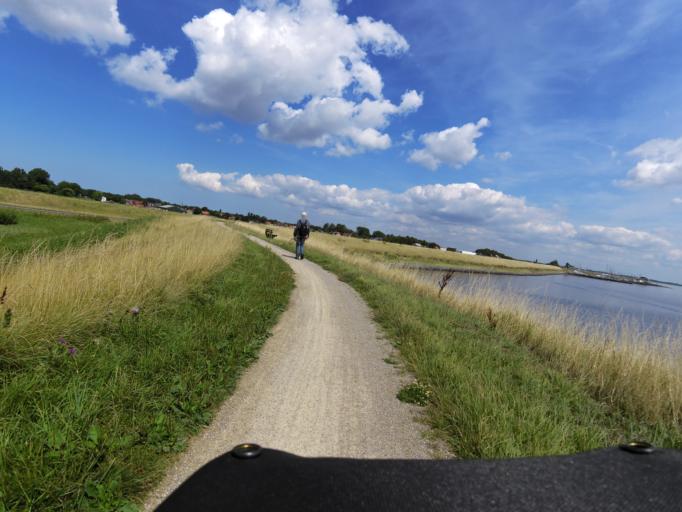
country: NL
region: South Holland
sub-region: Gemeente Goeree-Overflakkee
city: Ouddorp
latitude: 51.7970
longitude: 3.9248
